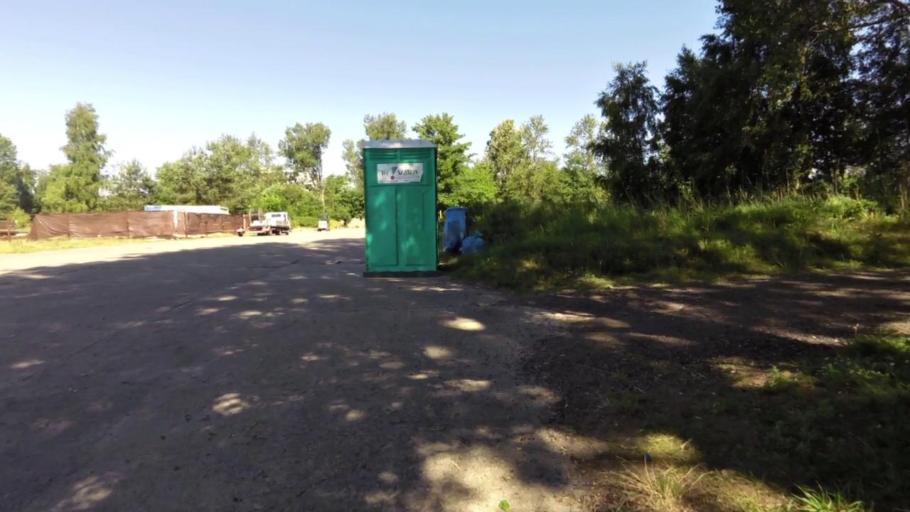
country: PL
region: West Pomeranian Voivodeship
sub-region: Powiat koszalinski
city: Mielno
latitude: 54.2754
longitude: 16.1187
